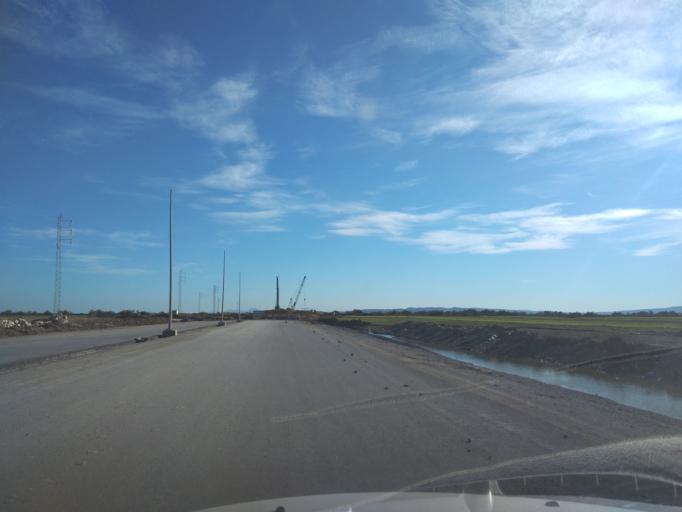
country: TN
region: Ariana
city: Qal'at al Andalus
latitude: 37.0267
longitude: 10.1387
